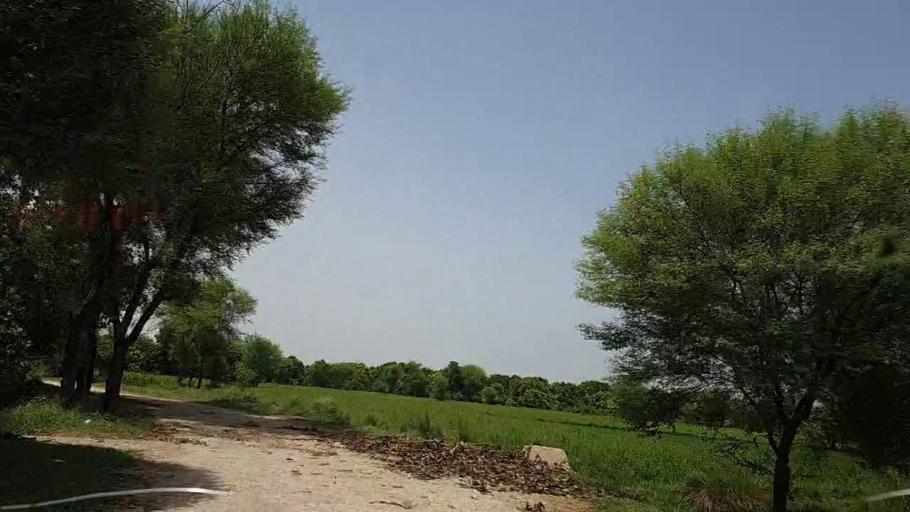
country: PK
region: Sindh
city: Tharu Shah
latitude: 26.9940
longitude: 68.0835
